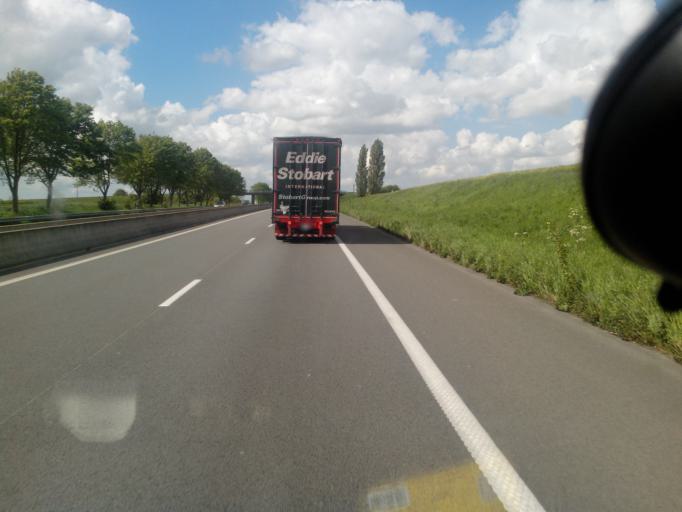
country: FR
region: Nord-Pas-de-Calais
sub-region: Departement du Nord
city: Godewaersvelde
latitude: 50.7768
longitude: 2.6302
